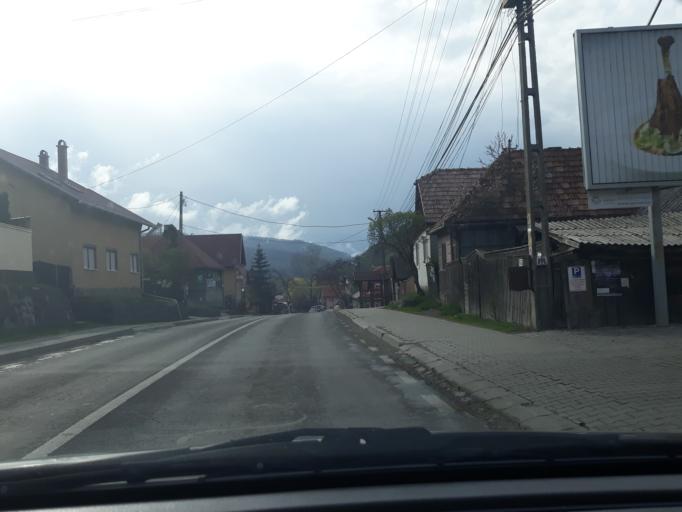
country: RO
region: Harghita
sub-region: Comuna Praid
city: Praid
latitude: 46.5511
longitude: 25.1227
